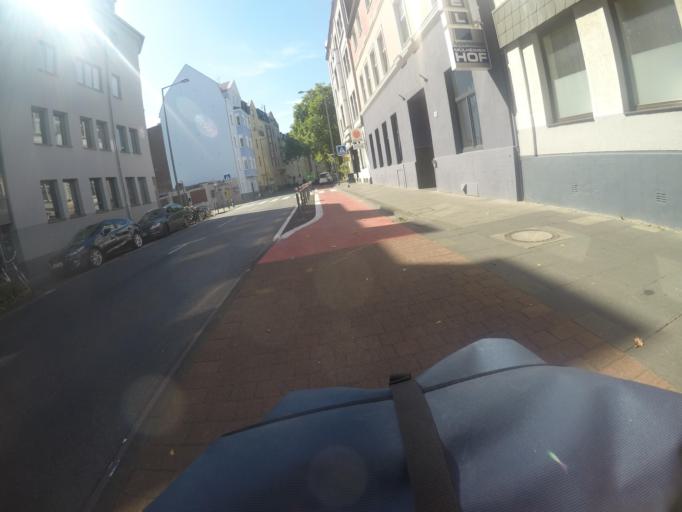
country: DE
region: North Rhine-Westphalia
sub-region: Regierungsbezirk Koln
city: Muelheim
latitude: 50.9602
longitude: 6.9964
